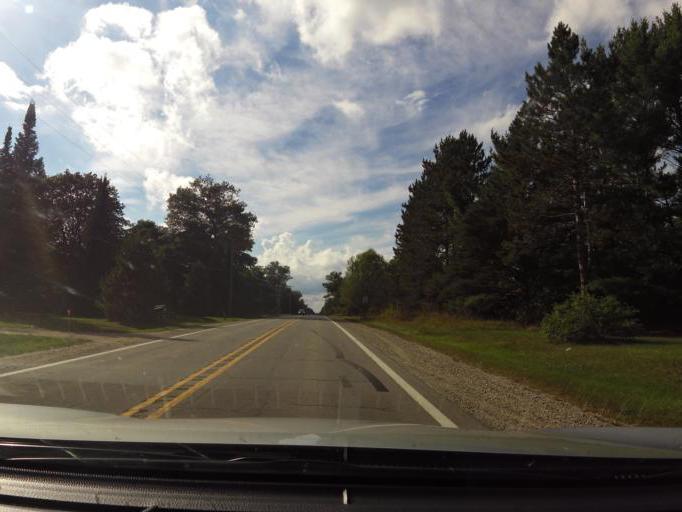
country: US
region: Michigan
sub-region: Roscommon County
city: Roscommon
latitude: 44.5109
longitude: -84.5532
